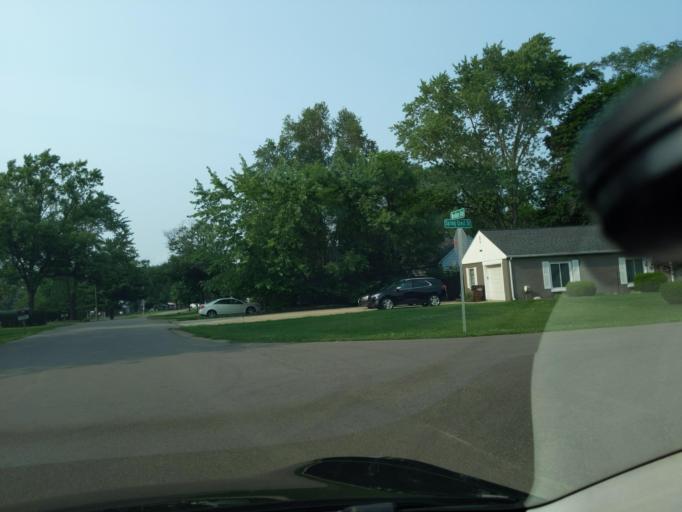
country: US
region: Michigan
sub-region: Jackson County
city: Jackson
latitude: 42.2382
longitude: -84.4472
